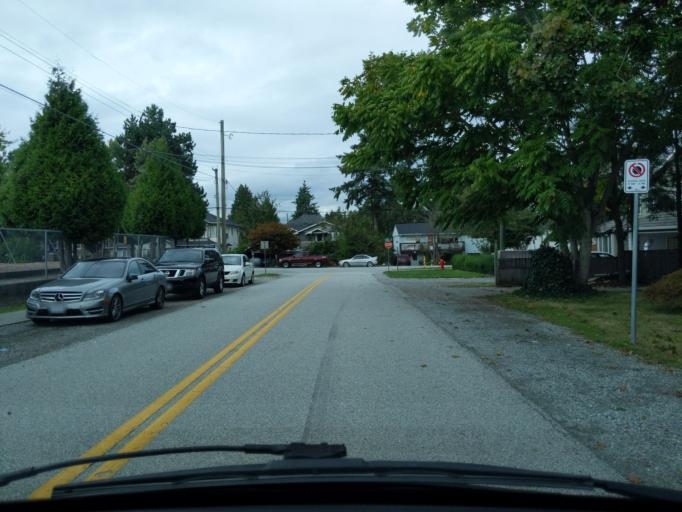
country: CA
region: British Columbia
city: New Westminster
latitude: 49.1949
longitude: -122.8580
